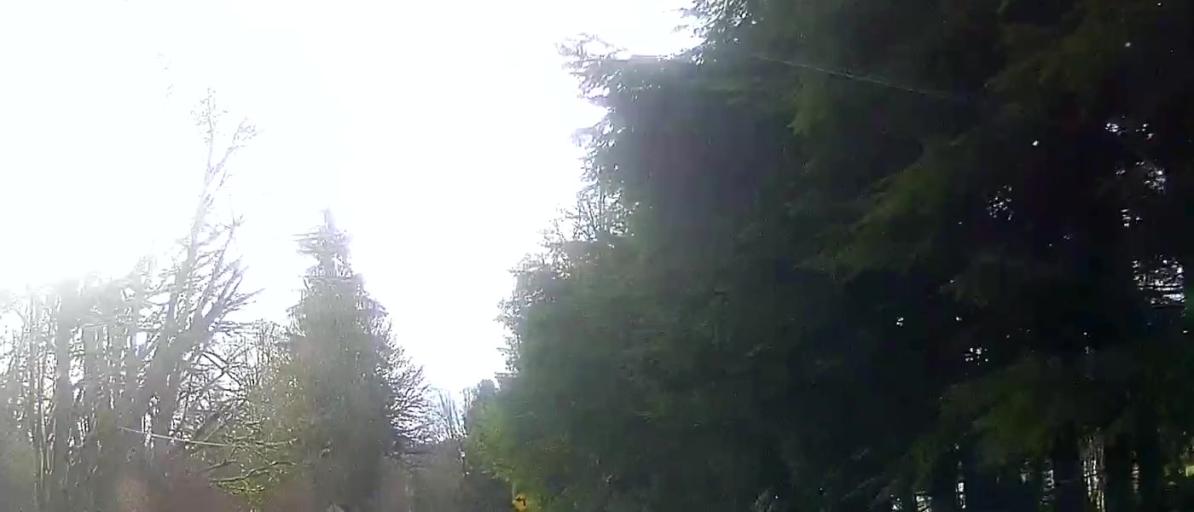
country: US
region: Washington
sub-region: Skagit County
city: Sedro-Woolley
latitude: 48.5711
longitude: -122.2982
